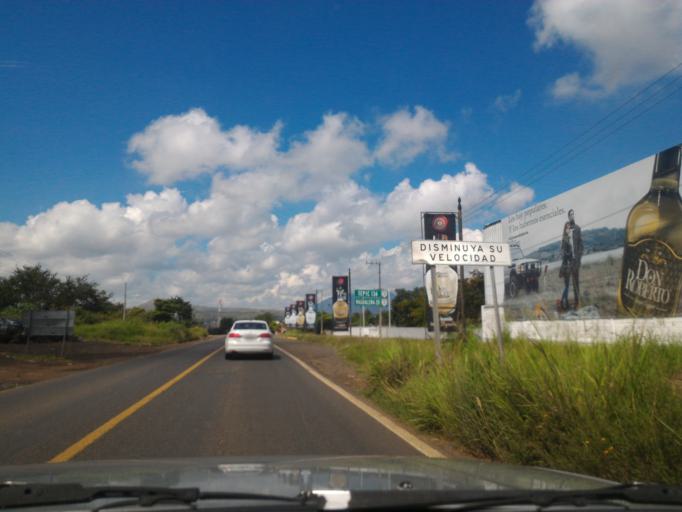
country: MX
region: Jalisco
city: Tequila
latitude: 20.8774
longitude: -103.8157
